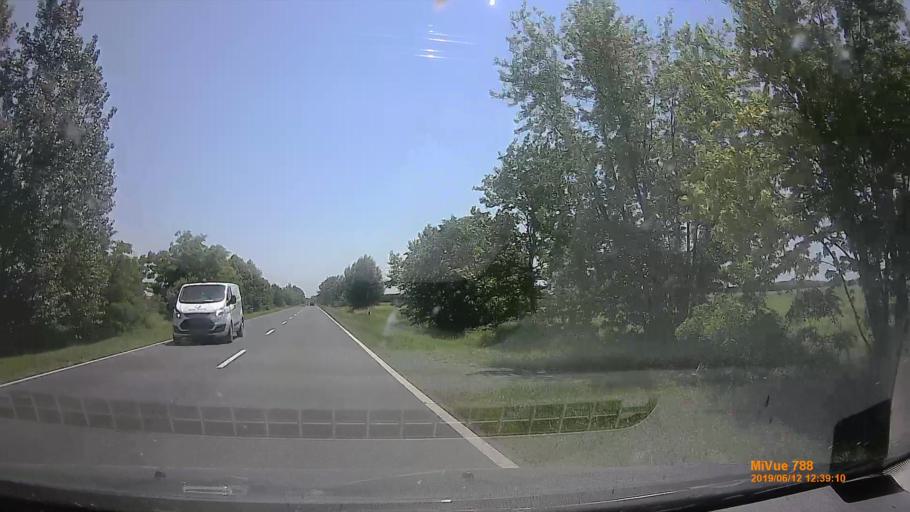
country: HU
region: Bacs-Kiskun
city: Kiskunfelegyhaza
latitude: 46.7697
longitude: 19.8078
